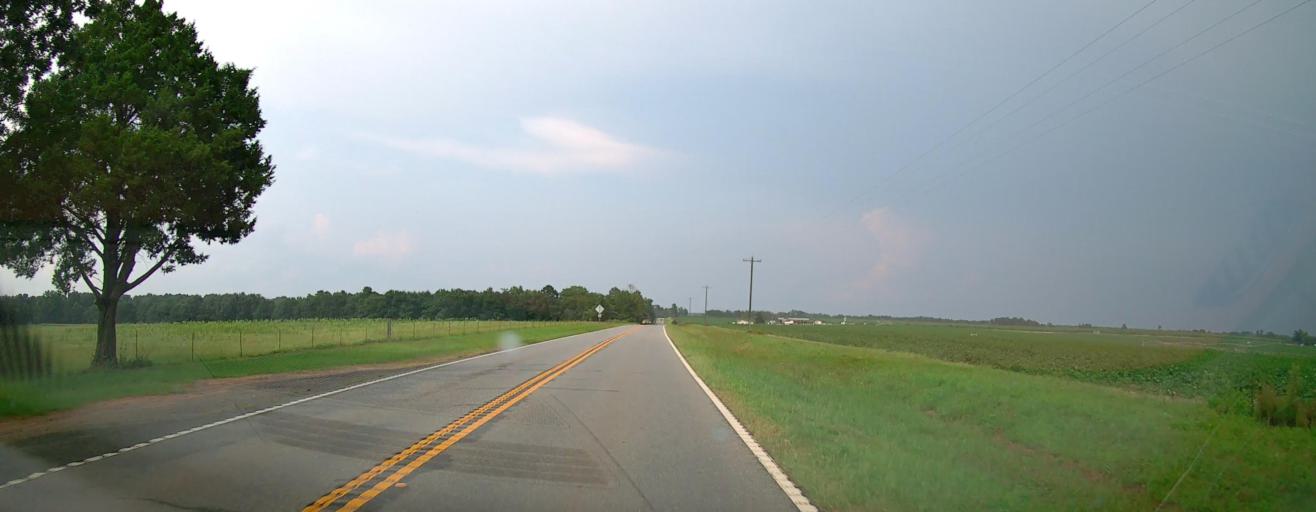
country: US
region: Georgia
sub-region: Twiggs County
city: Jeffersonville
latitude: 32.5803
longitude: -83.3914
